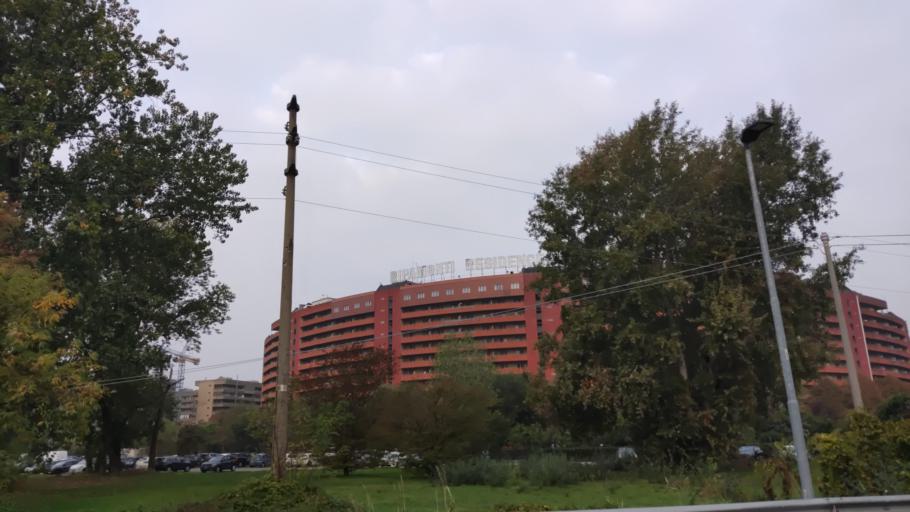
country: IT
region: Lombardy
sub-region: Citta metropolitana di Milano
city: Pieve Emanuele
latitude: 45.3471
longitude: 9.2017
